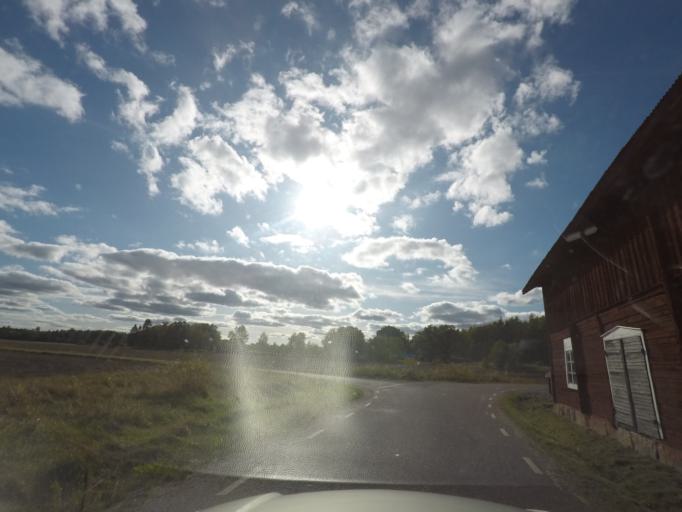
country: SE
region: Vaestmanland
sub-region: Hallstahammars Kommun
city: Kolback
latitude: 59.5144
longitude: 16.1864
